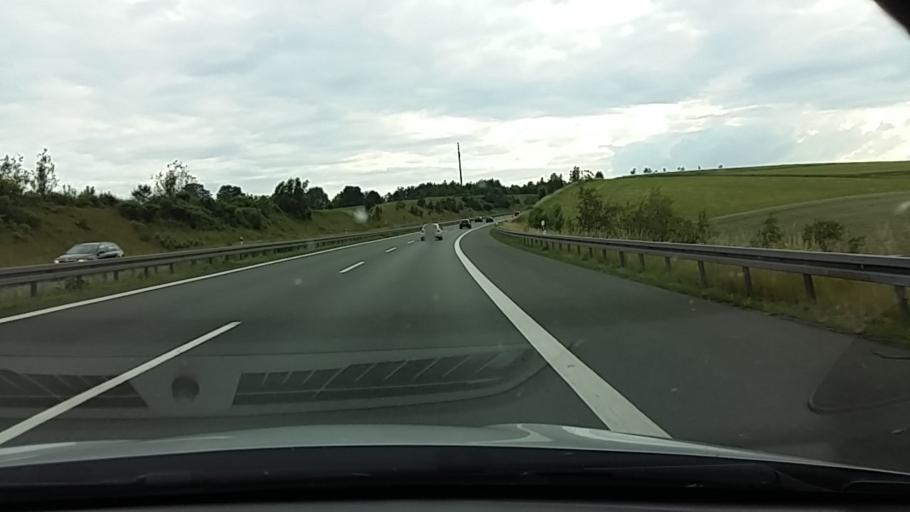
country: DE
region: Bavaria
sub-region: Upper Palatinate
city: Vohenstrauss
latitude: 49.5970
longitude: 12.3187
